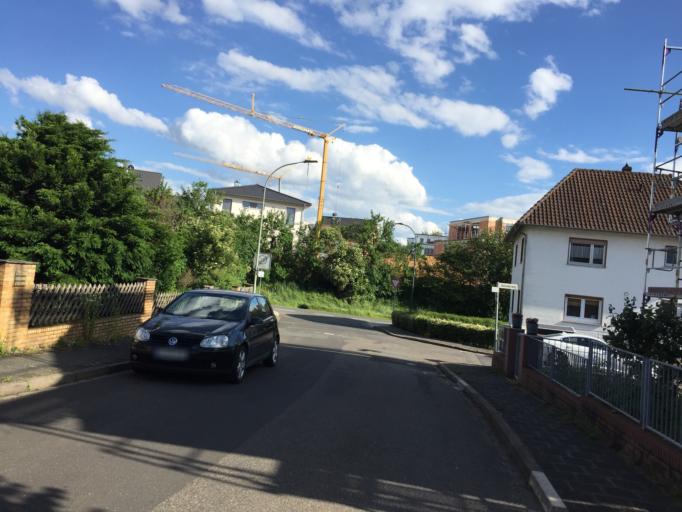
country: DE
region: Hesse
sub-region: Regierungsbezirk Darmstadt
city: Karben
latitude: 50.2390
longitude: 8.7756
